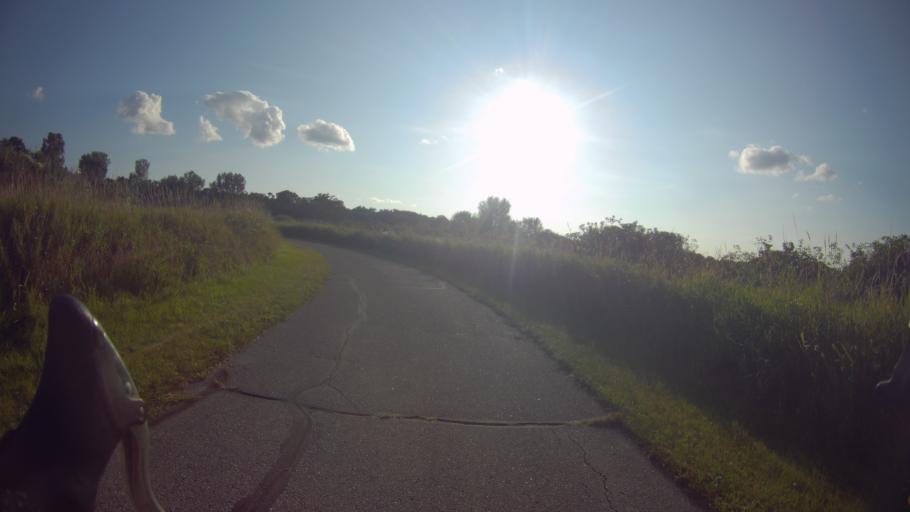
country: US
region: Wisconsin
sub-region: Dane County
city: Monona
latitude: 43.0232
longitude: -89.3599
